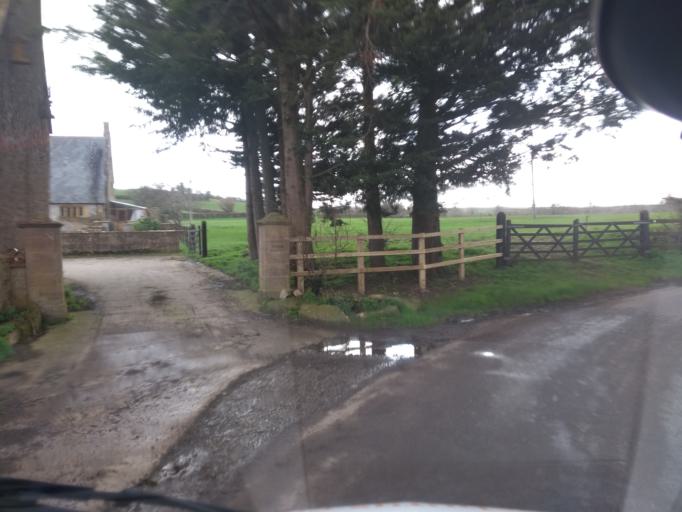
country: GB
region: England
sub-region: Somerset
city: South Petherton
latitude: 50.9801
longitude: -2.8439
